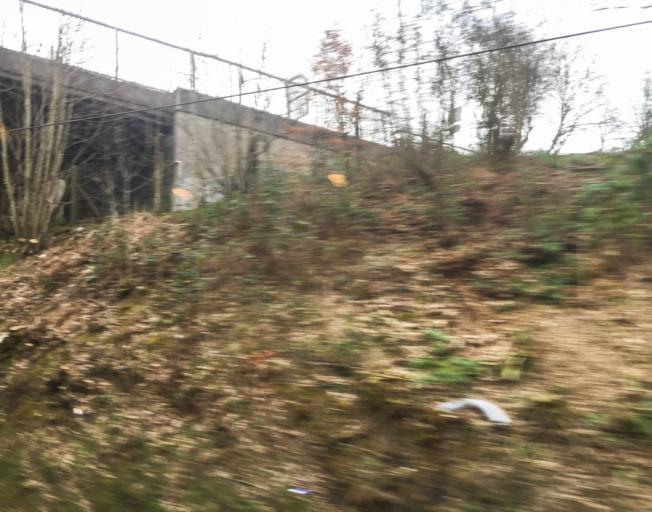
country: GB
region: Scotland
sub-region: West Dunbartonshire
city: Old Kilpatrick
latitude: 55.9229
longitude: -4.4509
